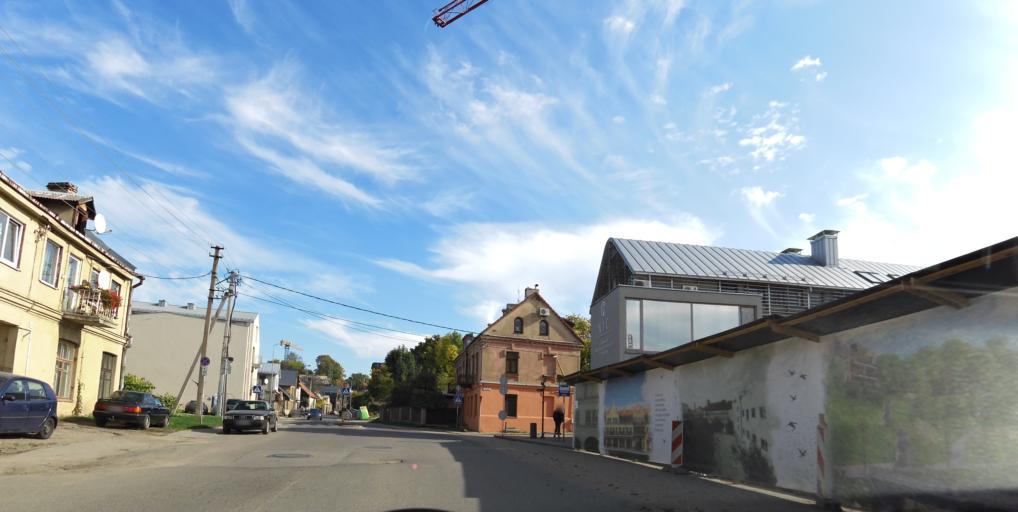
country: LT
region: Vilnius County
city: Rasos
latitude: 54.6815
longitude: 25.3052
